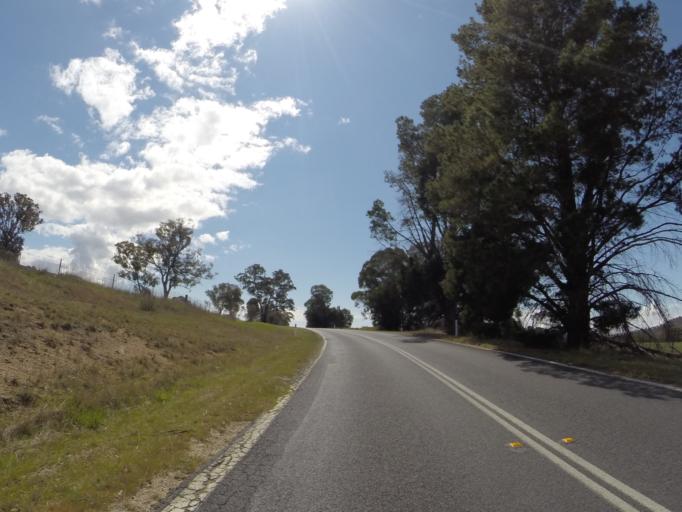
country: AU
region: Australian Capital Territory
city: Macquarie
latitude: -35.3806
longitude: 148.9622
